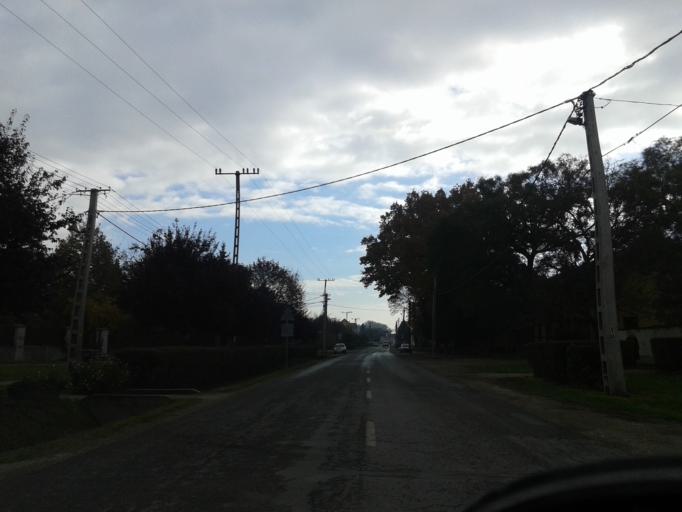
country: HU
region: Fejer
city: Adony
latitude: 47.1215
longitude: 18.8616
